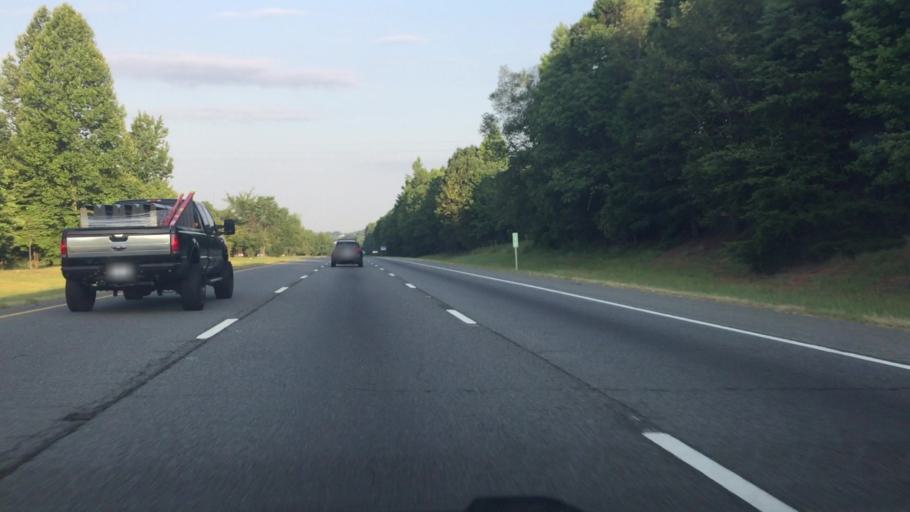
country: US
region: North Carolina
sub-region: Davidson County
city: Lexington
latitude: 35.7770
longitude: -80.2799
